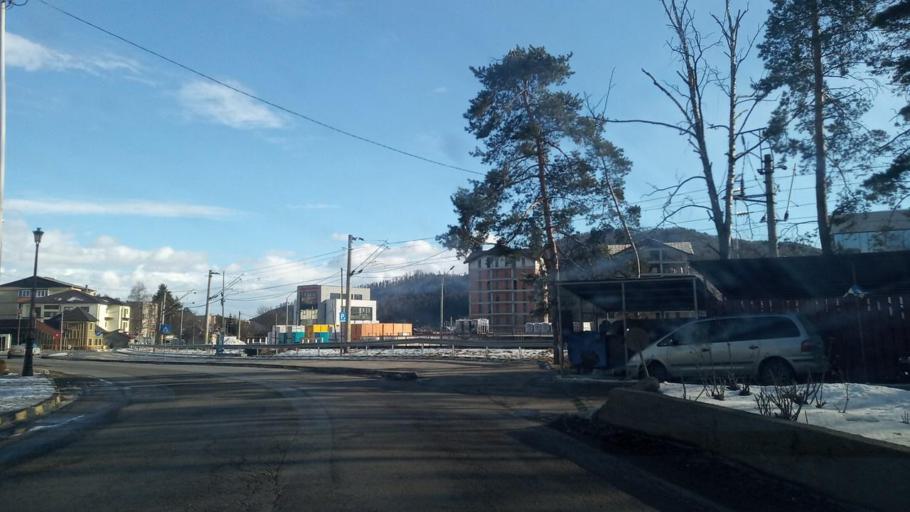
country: RO
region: Suceava
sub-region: Oras Gura Humorului
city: Gura Humorului
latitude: 47.5532
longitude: 25.8881
